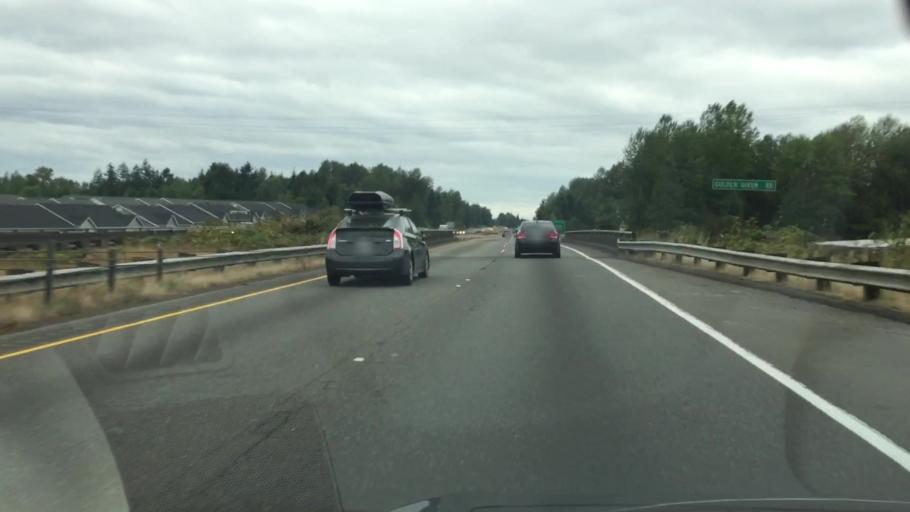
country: US
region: Washington
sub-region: Pierce County
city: Midland
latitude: 47.1593
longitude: -122.4151
